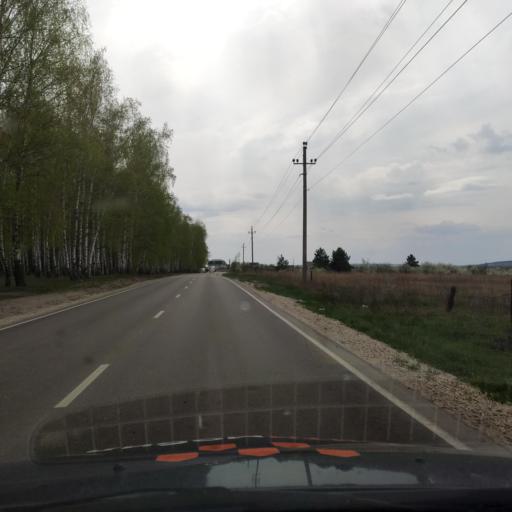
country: RU
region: Voronezj
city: Podgornoye
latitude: 51.8430
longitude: 39.1446
